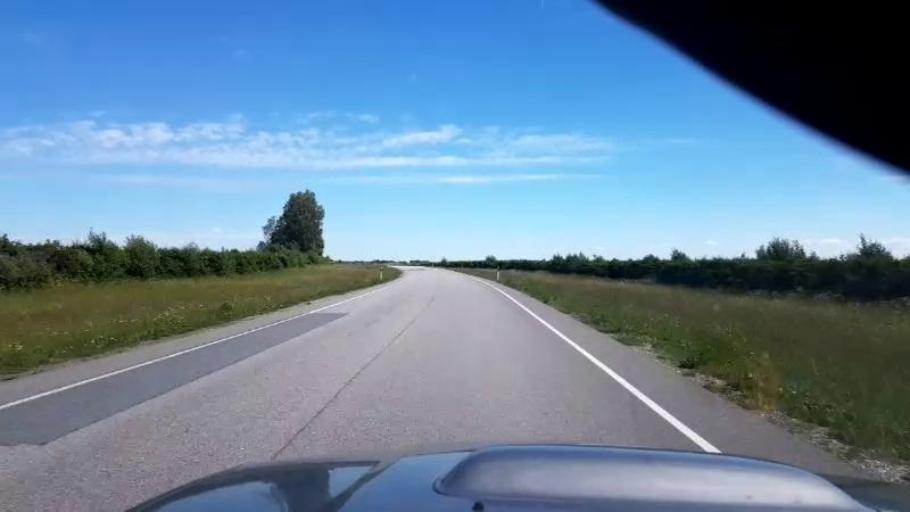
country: EE
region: Jaervamaa
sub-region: Koeru vald
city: Koeru
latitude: 58.9784
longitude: 26.0636
